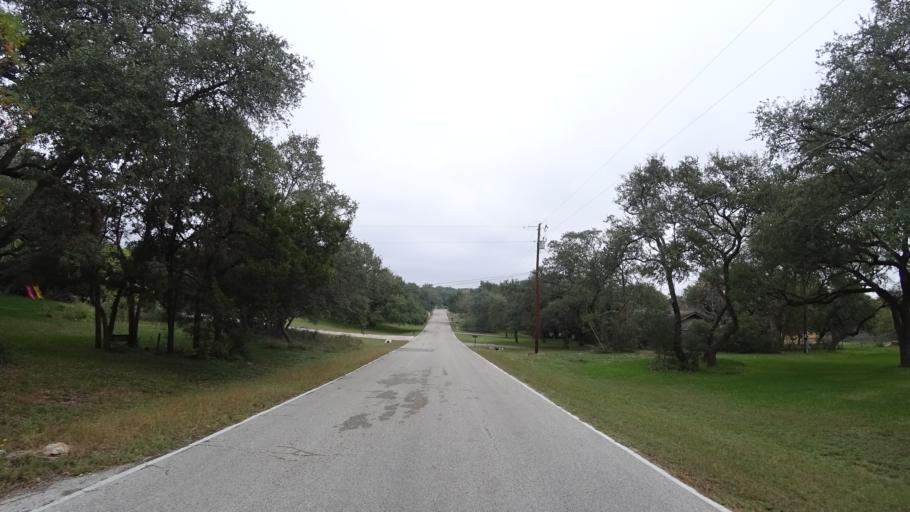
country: US
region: Texas
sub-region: Travis County
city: Barton Creek
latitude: 30.2240
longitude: -97.8973
